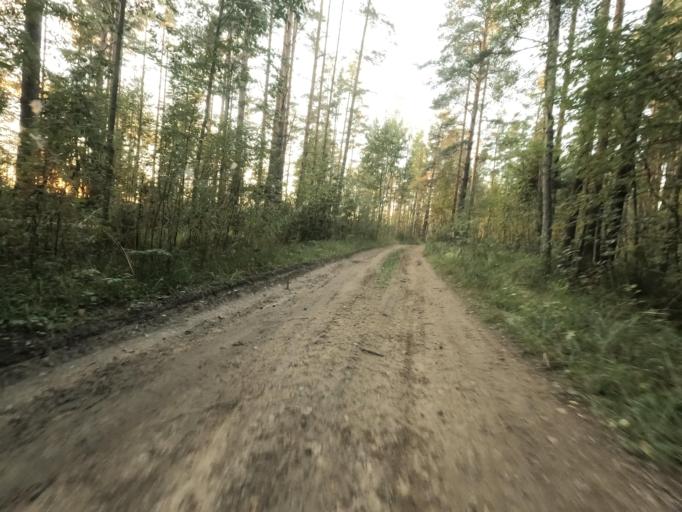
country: RU
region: Leningrad
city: Otradnoye
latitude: 59.8400
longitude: 30.8036
